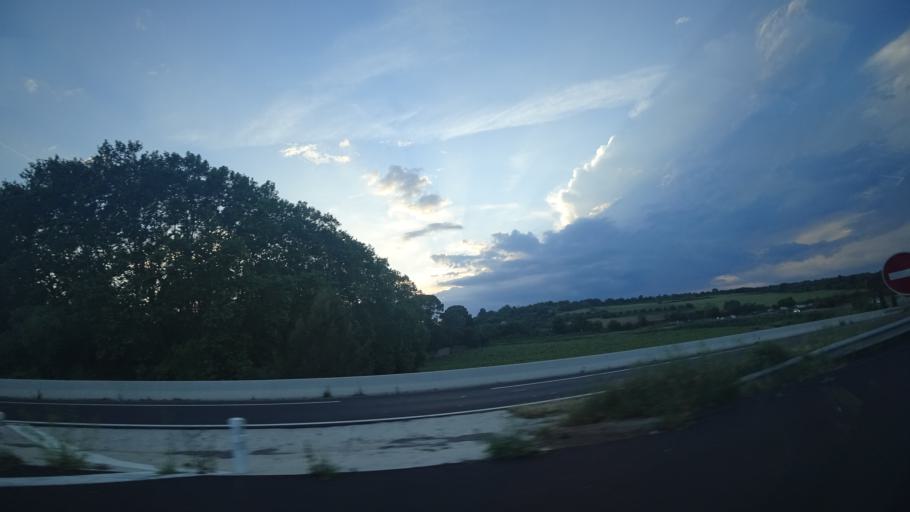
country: FR
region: Languedoc-Roussillon
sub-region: Departement de l'Herault
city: Lezignan-la-Cebe
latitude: 43.4750
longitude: 3.4366
